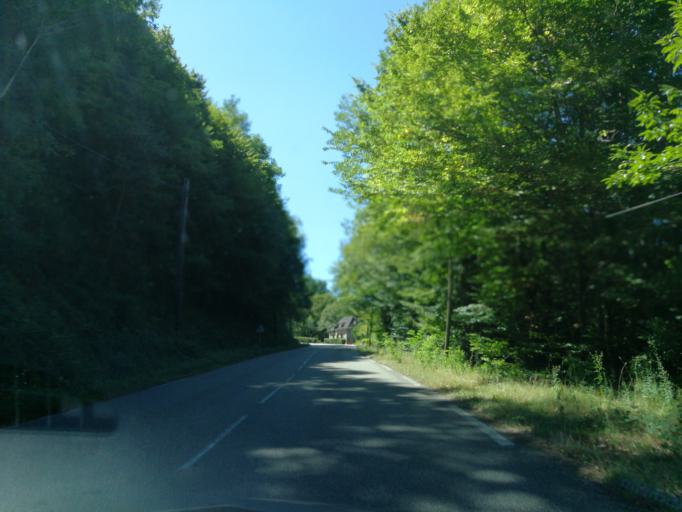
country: FR
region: Limousin
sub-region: Departement de la Correze
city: Argentat
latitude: 45.0789
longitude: 1.9447
